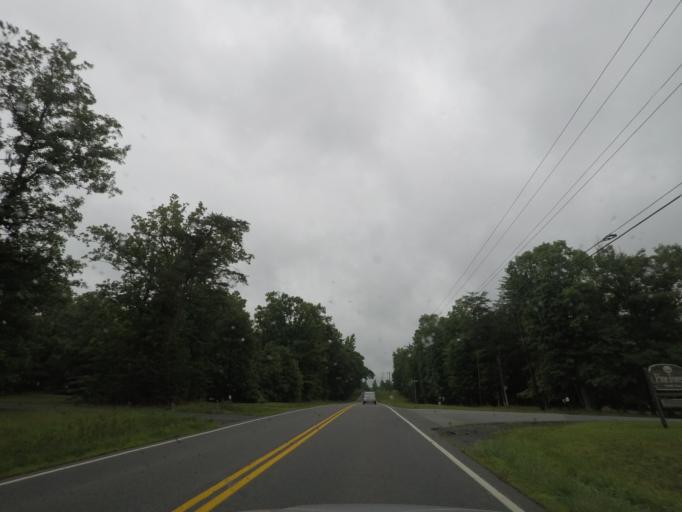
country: US
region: Virginia
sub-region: Fluvanna County
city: Palmyra
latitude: 37.9279
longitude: -78.2498
